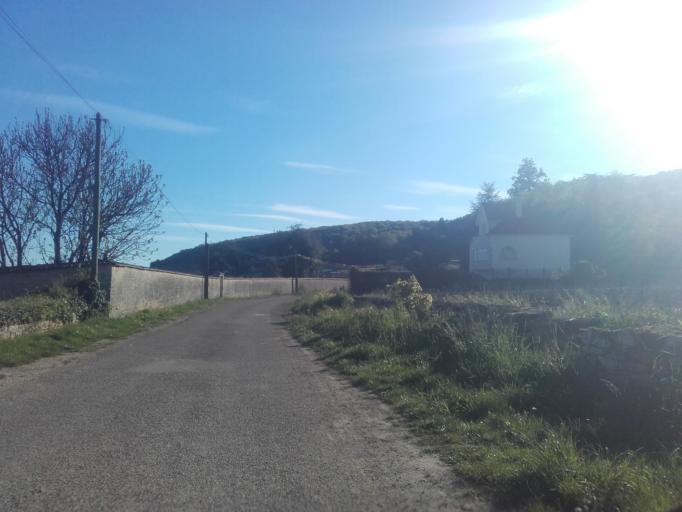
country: FR
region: Bourgogne
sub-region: Departement de Saone-et-Loire
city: Rully
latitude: 46.8764
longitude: 4.7356
